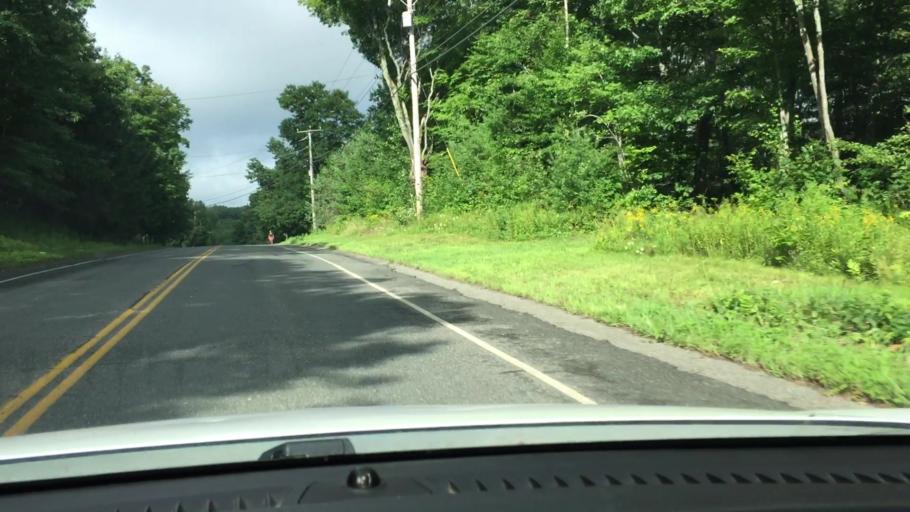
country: US
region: Massachusetts
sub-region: Berkshire County
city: Hinsdale
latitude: 42.4449
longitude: -73.0842
